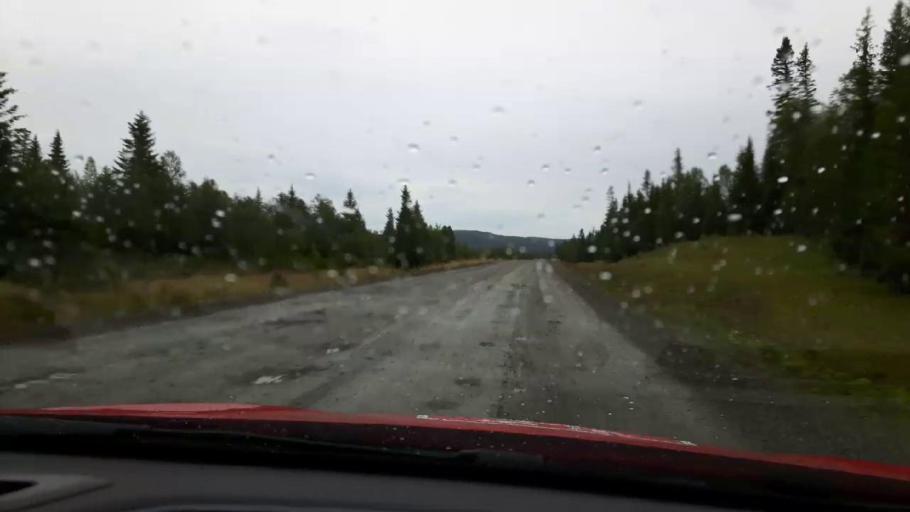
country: NO
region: Nord-Trondelag
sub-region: Meraker
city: Meraker
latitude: 63.5600
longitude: 12.3022
